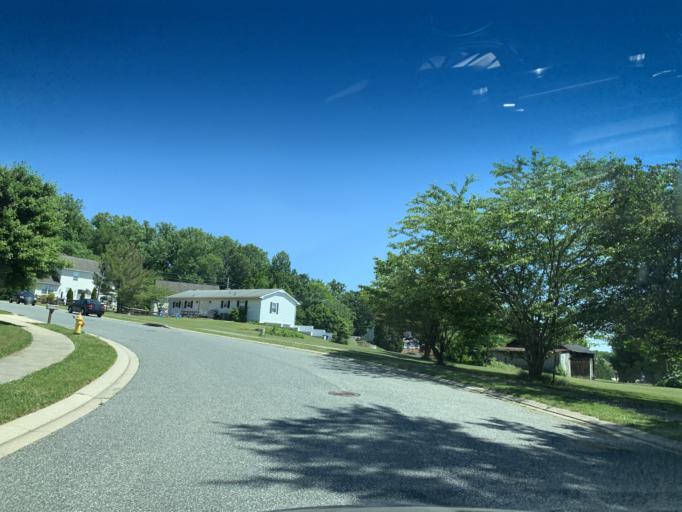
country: US
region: Maryland
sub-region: Harford County
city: Aberdeen
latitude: 39.5159
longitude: -76.1888
